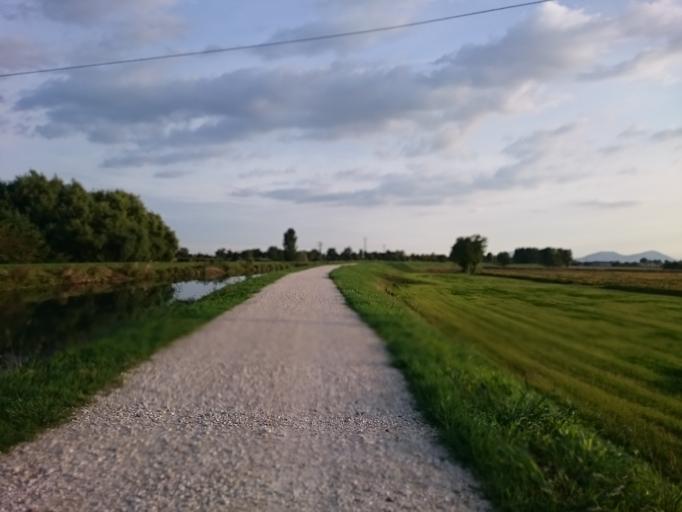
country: IT
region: Veneto
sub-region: Provincia di Padova
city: Campodoro
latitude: 45.4975
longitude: 11.7341
